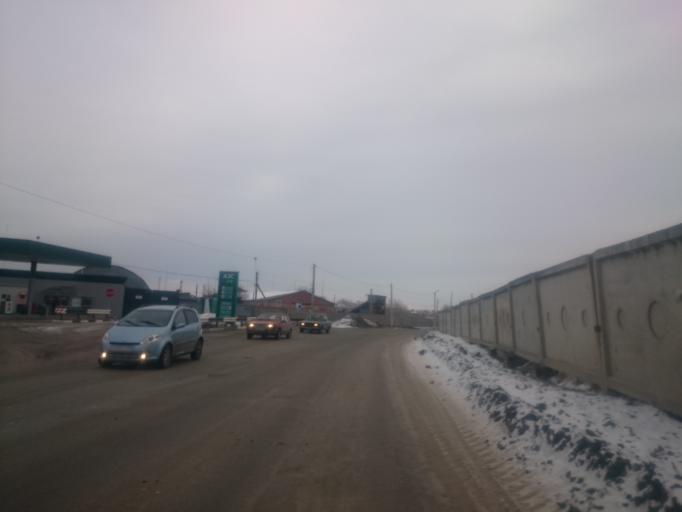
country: RU
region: Sverdlovsk
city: Irbit
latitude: 57.6651
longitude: 63.0619
